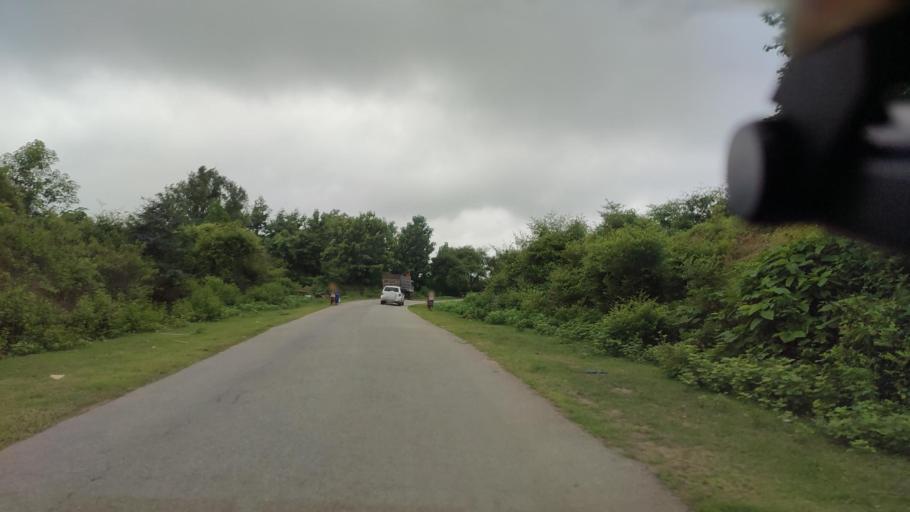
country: MM
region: Mandalay
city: Nay Pyi Taw
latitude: 19.9969
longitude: 95.9241
